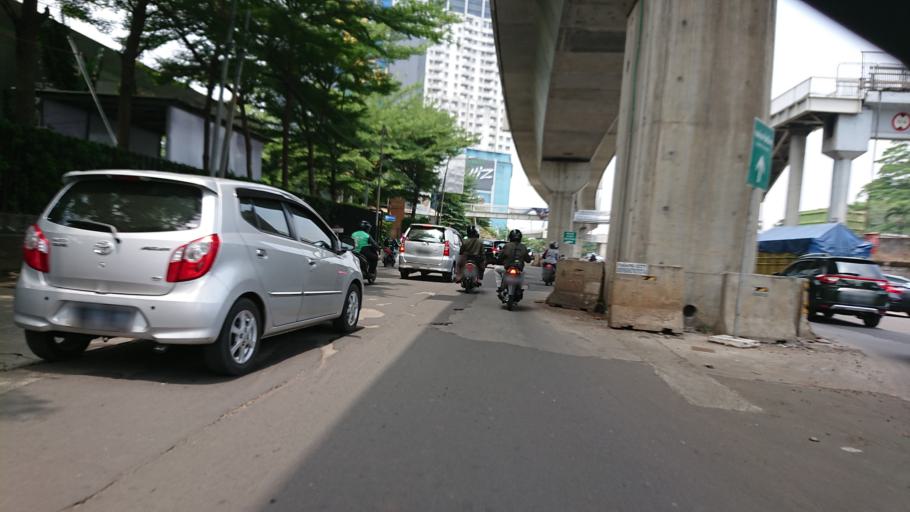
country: ID
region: Banten
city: South Tangerang
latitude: -6.2906
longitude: 106.7804
